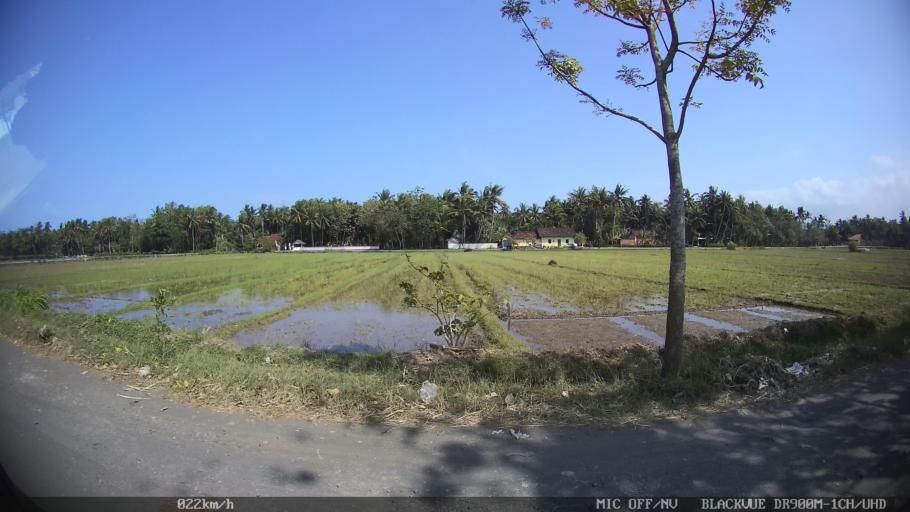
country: ID
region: Daerah Istimewa Yogyakarta
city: Srandakan
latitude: -7.9576
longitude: 110.2163
